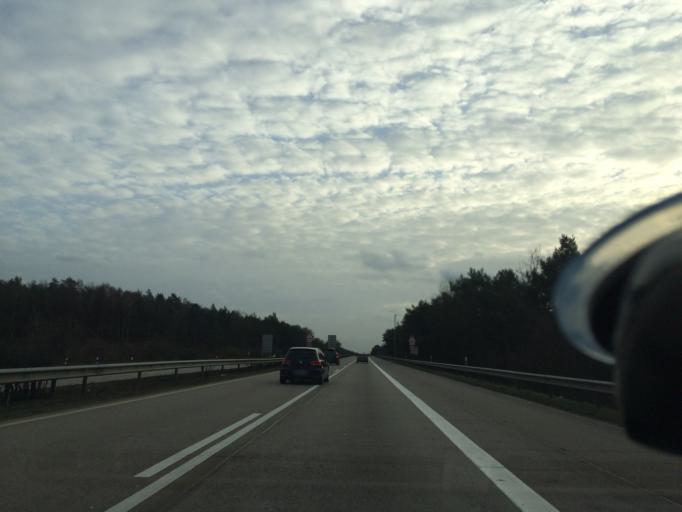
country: DE
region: Lower Saxony
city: Soltau
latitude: 52.9974
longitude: 9.9286
